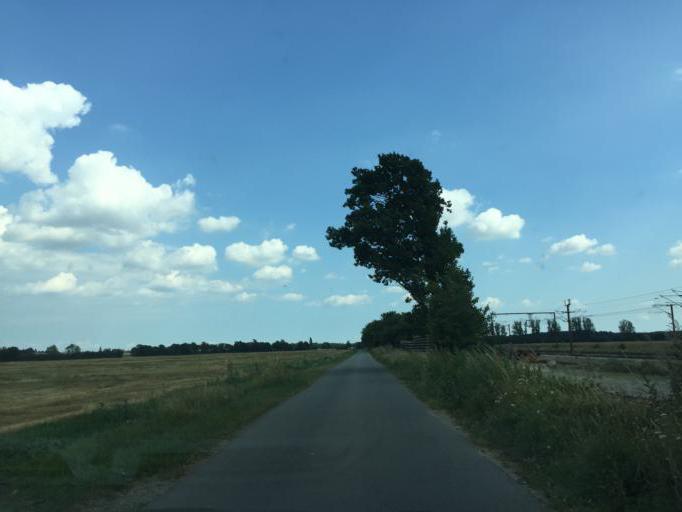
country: DK
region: South Denmark
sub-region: Kerteminde Kommune
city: Langeskov
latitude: 55.3776
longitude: 10.5297
